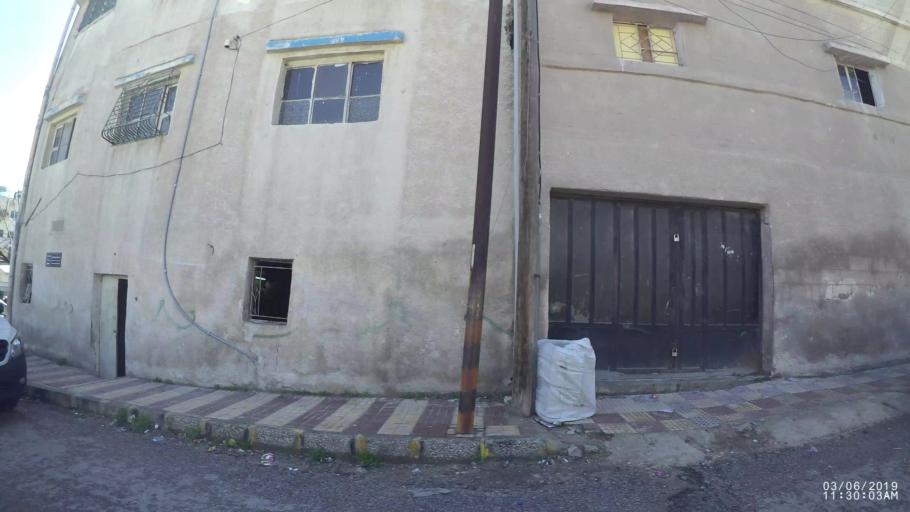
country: JO
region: Amman
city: Amman
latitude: 31.9817
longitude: 35.9930
